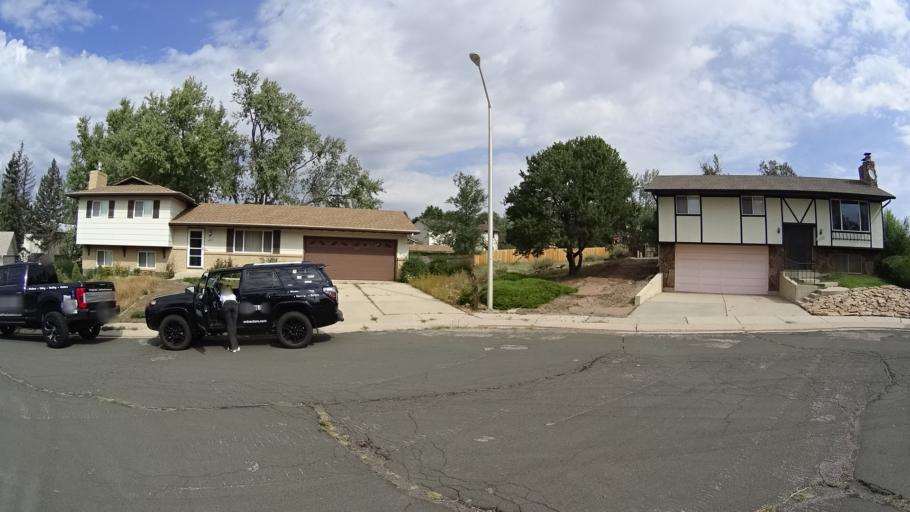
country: US
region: Colorado
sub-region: El Paso County
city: Cimarron Hills
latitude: 38.8543
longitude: -104.7285
